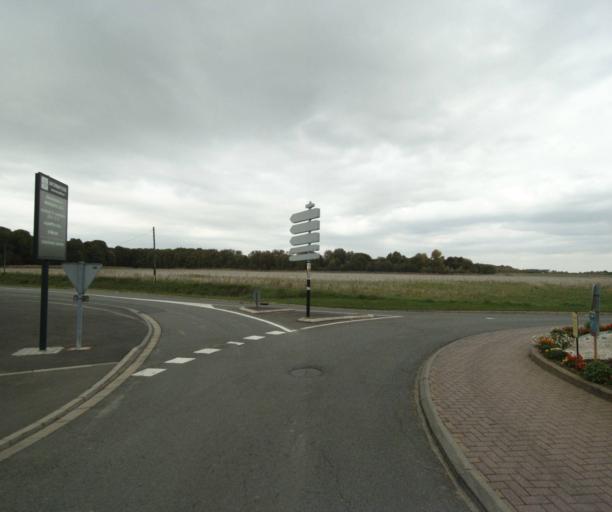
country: FR
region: Nord-Pas-de-Calais
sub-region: Departement du Nord
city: Marquillies
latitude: 50.5587
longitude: 2.8706
